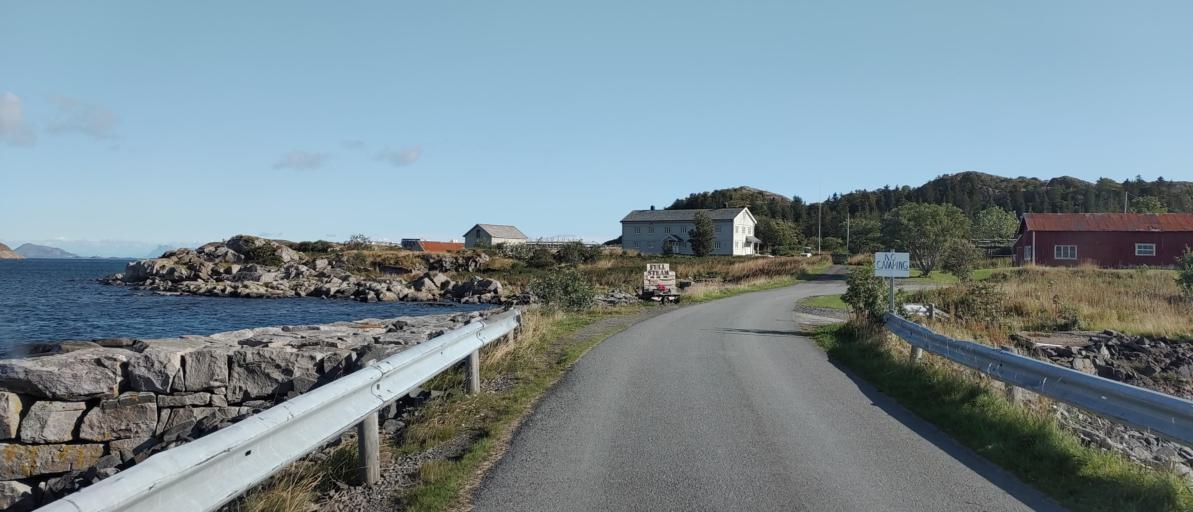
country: NO
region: Nordland
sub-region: Vagan
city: Kabelvag
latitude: 68.1606
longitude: 14.2216
